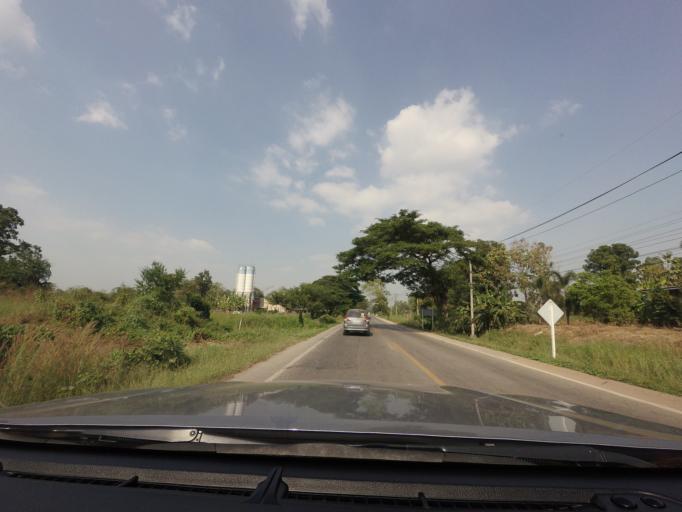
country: TH
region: Sukhothai
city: Kong Krailat
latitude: 16.9319
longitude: 99.9647
